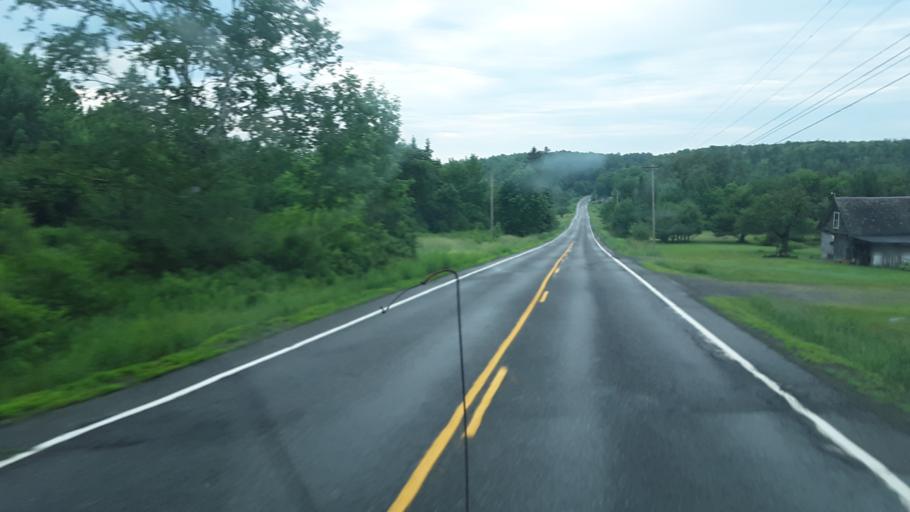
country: US
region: Maine
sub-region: Penobscot County
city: Patten
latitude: 46.0776
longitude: -68.4348
